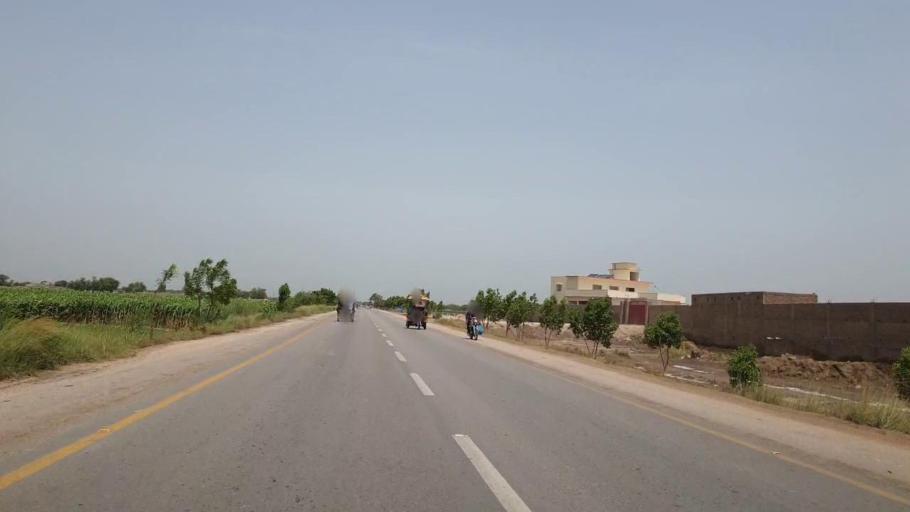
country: PK
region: Sindh
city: Nawabshah
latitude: 26.2316
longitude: 68.4838
